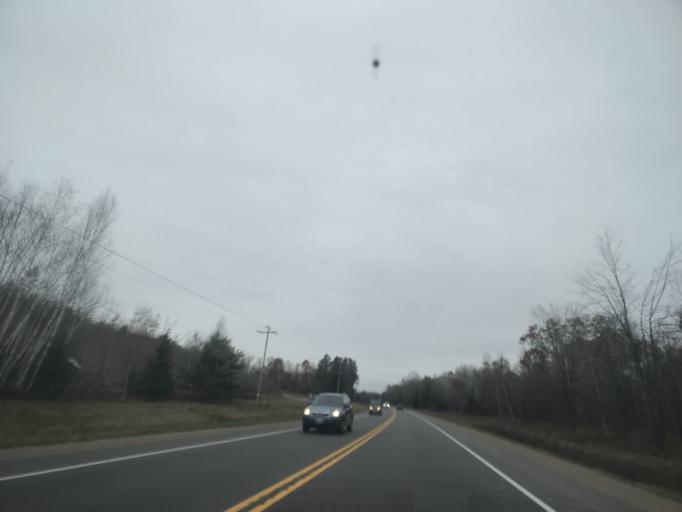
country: US
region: Wisconsin
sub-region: Menominee County
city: Legend Lake
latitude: 45.2917
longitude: -88.5112
